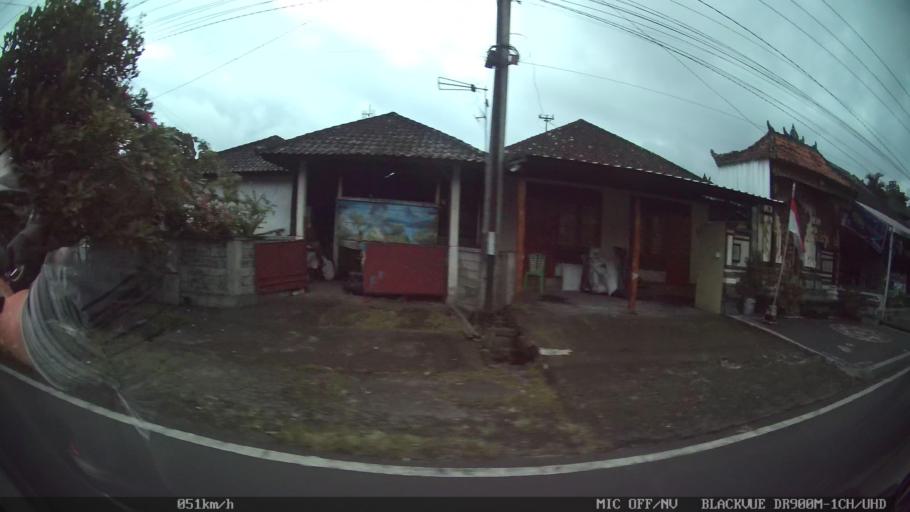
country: ID
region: Bali
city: Penebel
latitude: -8.4195
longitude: 115.1457
